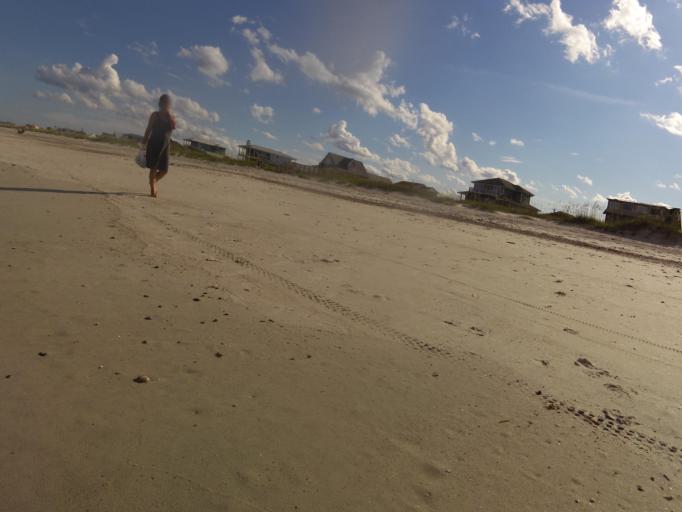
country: US
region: Florida
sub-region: Nassau County
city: Fernandina Beach
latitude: 30.6776
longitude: -81.4287
